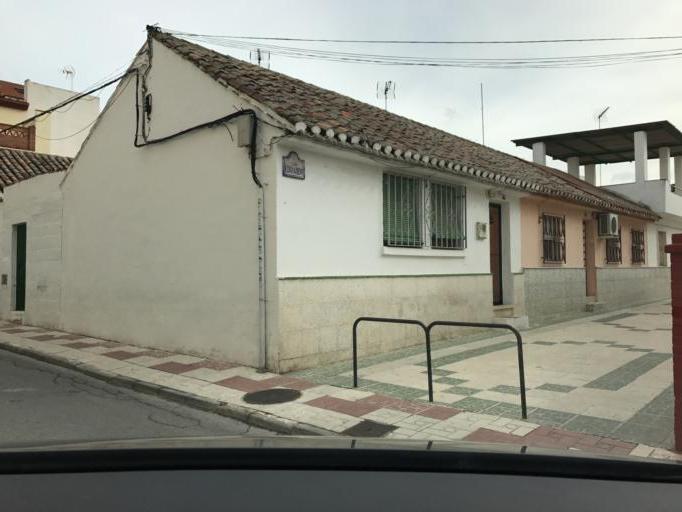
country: ES
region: Andalusia
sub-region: Provincia de Granada
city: Maracena
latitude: 37.2094
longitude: -3.6375
